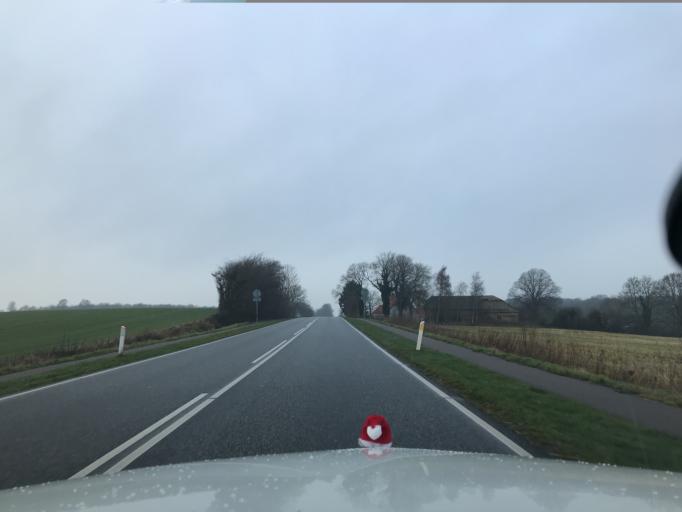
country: DK
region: South Denmark
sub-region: Sonderborg Kommune
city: Dybbol
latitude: 54.9102
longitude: 9.7133
